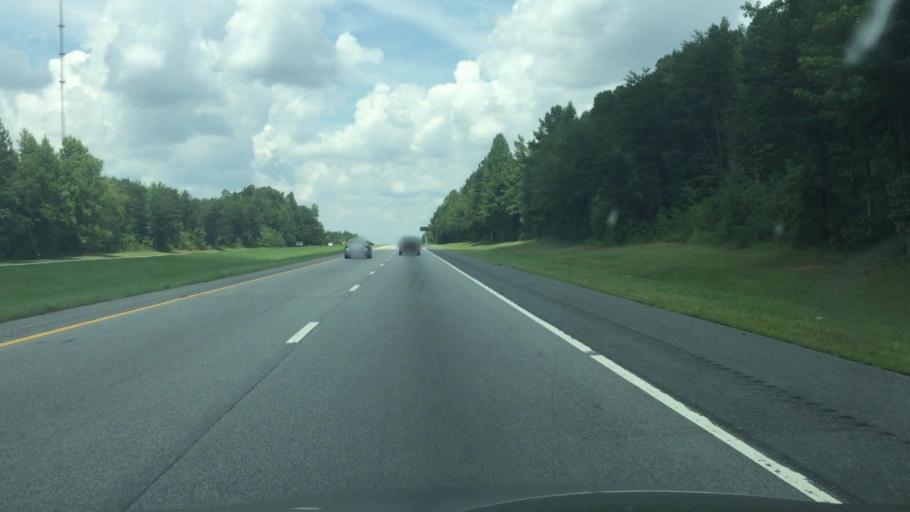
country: US
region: North Carolina
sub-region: Guilford County
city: Pleasant Garden
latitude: 35.9607
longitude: -79.8202
